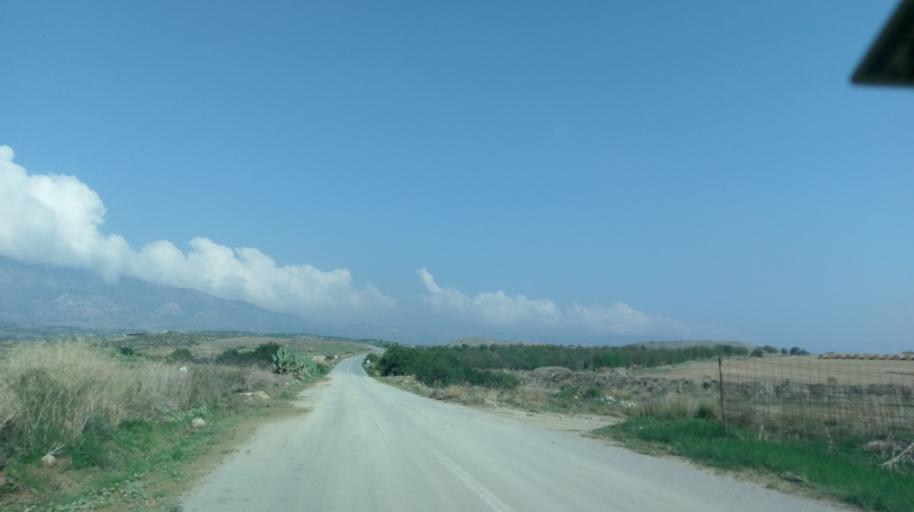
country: CY
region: Ammochostos
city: Lefkonoiko
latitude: 35.2623
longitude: 33.6096
